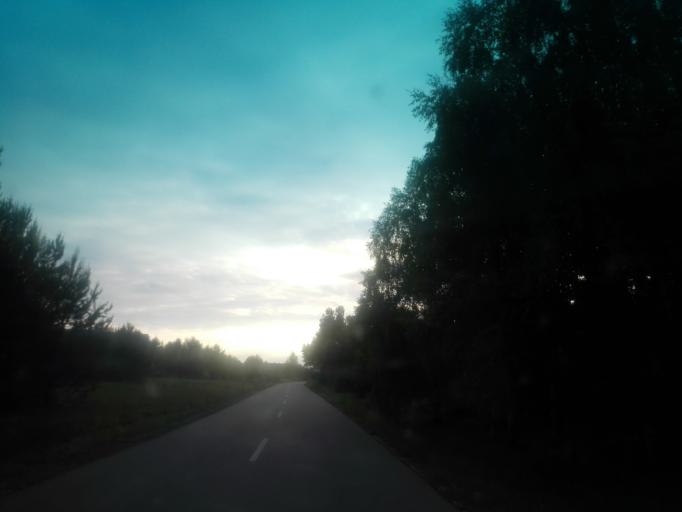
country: PL
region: Silesian Voivodeship
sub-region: Powiat czestochowski
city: Potok Zloty
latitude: 50.6929
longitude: 19.3882
